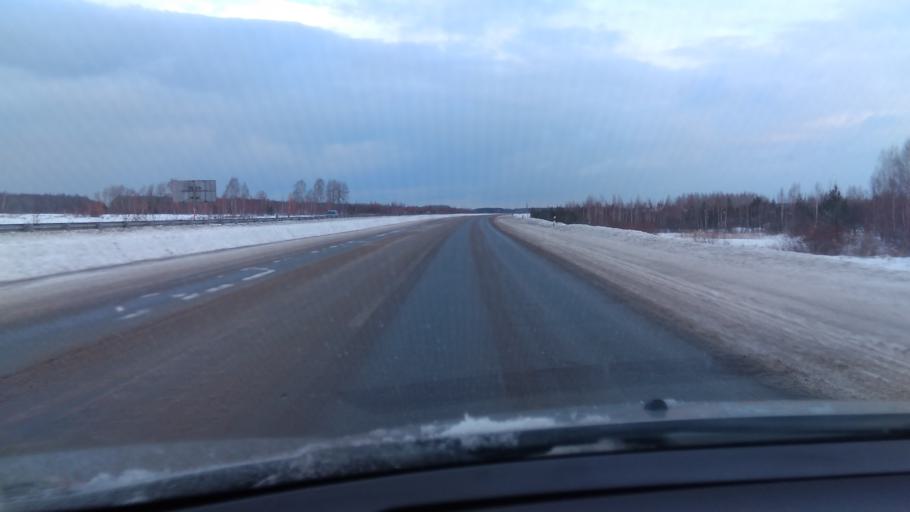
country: RU
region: Sverdlovsk
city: Nev'yansk
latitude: 57.5157
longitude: 60.1788
